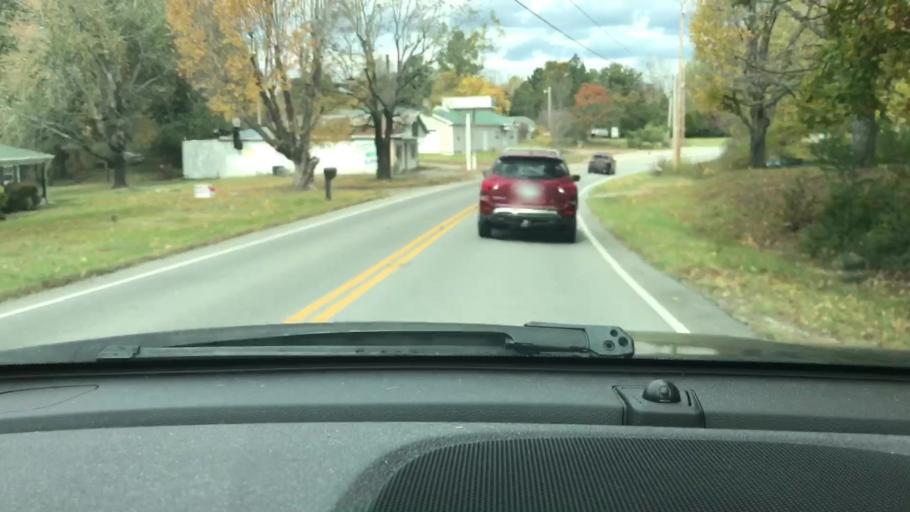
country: US
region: Tennessee
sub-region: Dickson County
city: Charlotte
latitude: 36.2412
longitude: -87.2455
